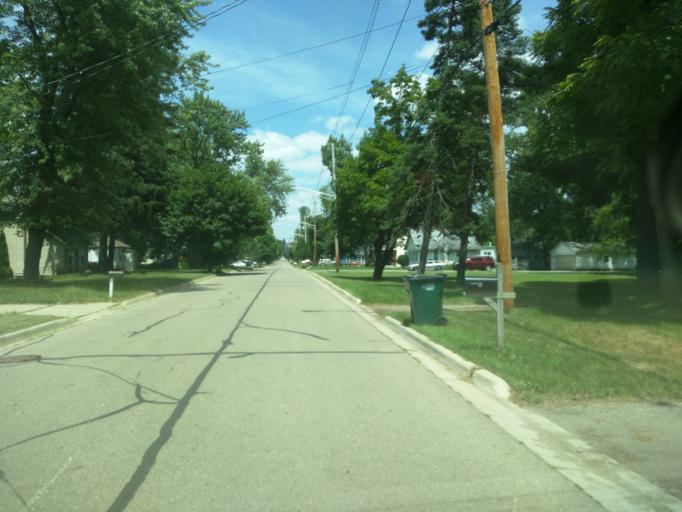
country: US
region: Michigan
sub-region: Ingham County
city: Lansing
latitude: 42.7653
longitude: -84.5518
